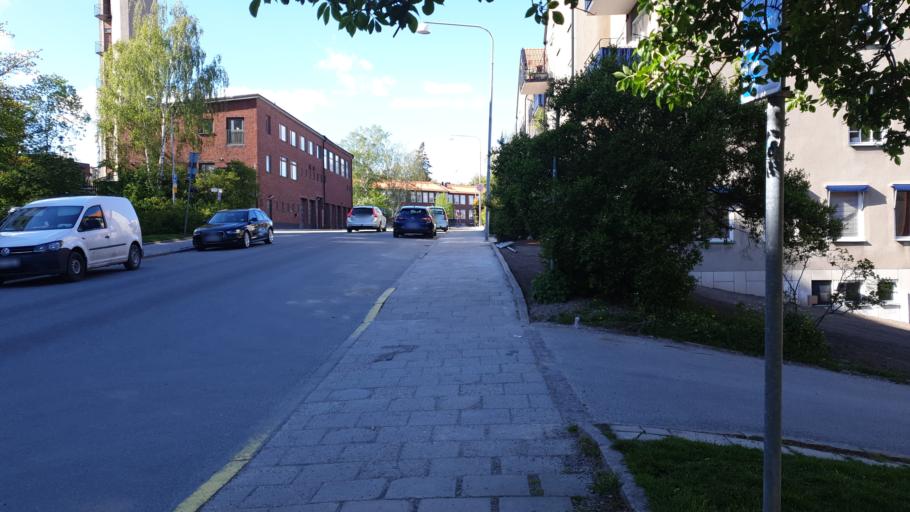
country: SE
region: Stockholm
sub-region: Solna Kommun
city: Rasunda
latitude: 59.3609
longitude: 17.9895
